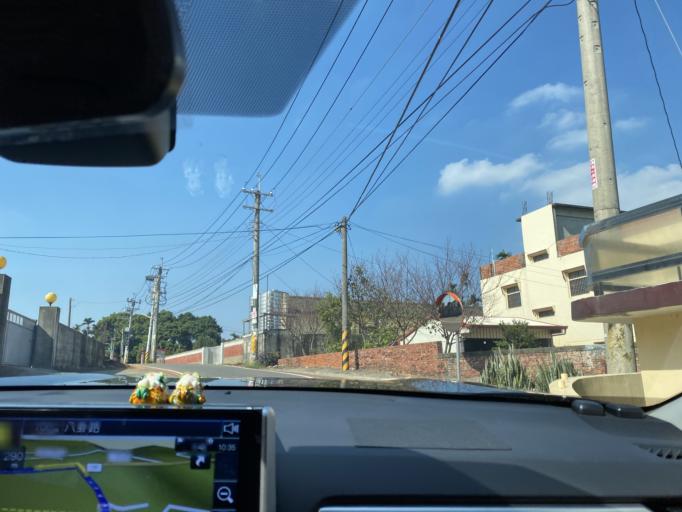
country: TW
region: Taiwan
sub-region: Nantou
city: Nantou
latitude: 23.9357
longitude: 120.6392
